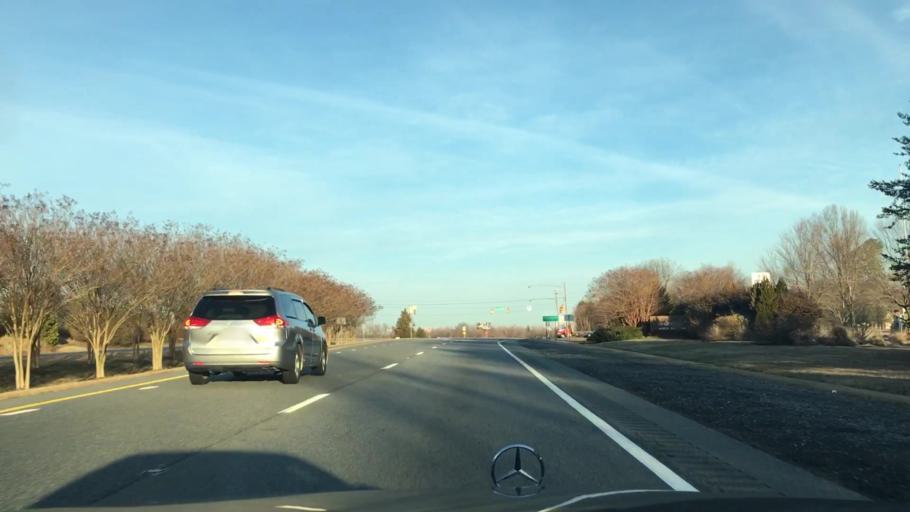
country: US
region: North Carolina
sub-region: Guilford County
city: Greensboro
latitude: 36.0269
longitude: -79.7689
